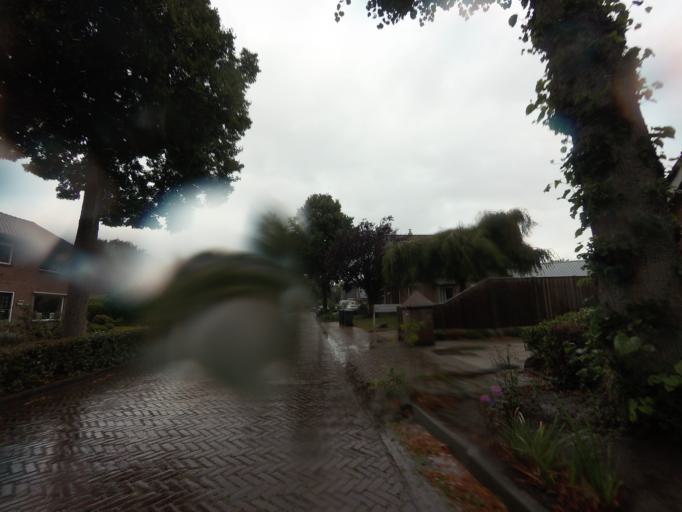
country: NL
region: Drenthe
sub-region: Gemeente Hoogeveen
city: Hoogeveen
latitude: 52.6397
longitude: 6.4471
